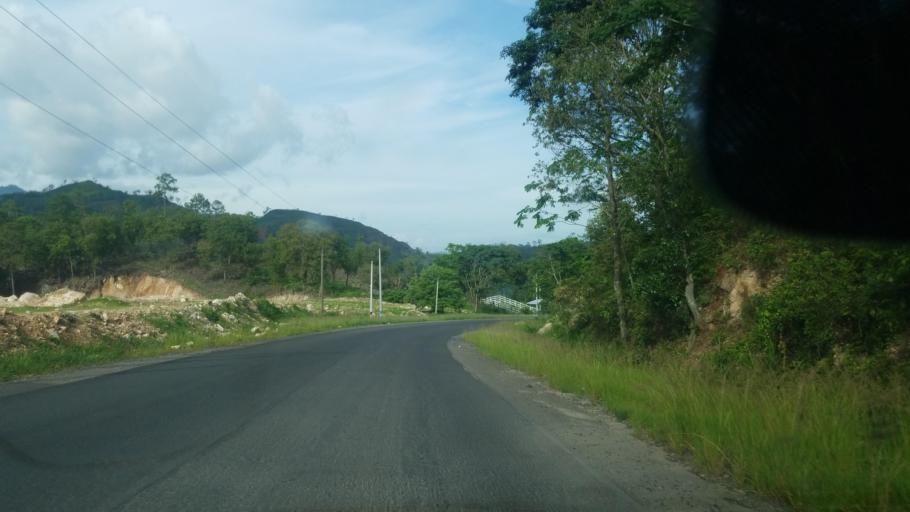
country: HN
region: Santa Barbara
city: Trinidad
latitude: 15.1705
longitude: -88.2627
